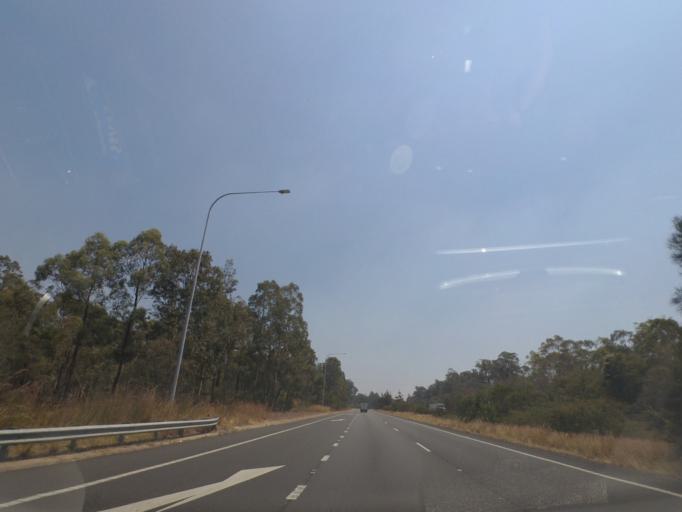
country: AU
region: New South Wales
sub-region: Newcastle
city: Beresfield
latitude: -32.8327
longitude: 151.6346
